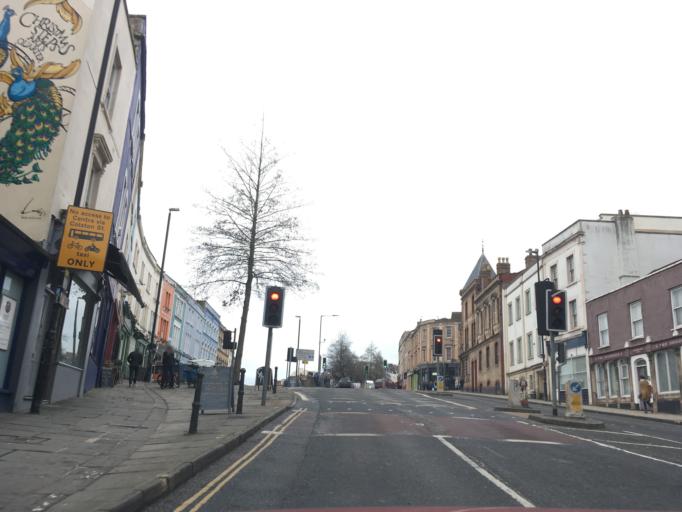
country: GB
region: England
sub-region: Bristol
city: Bristol
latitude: 51.4575
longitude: -2.5968
